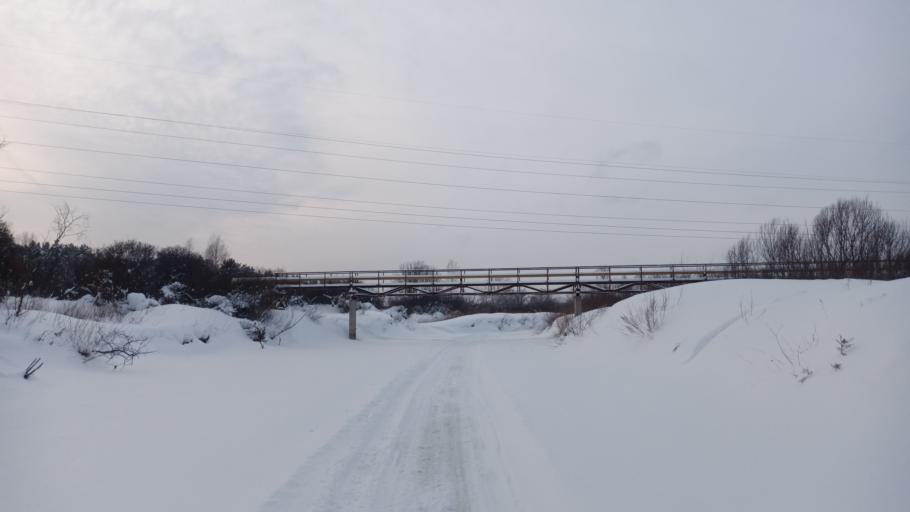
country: RU
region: Altai Krai
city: Yuzhnyy
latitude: 53.3070
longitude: 83.7155
